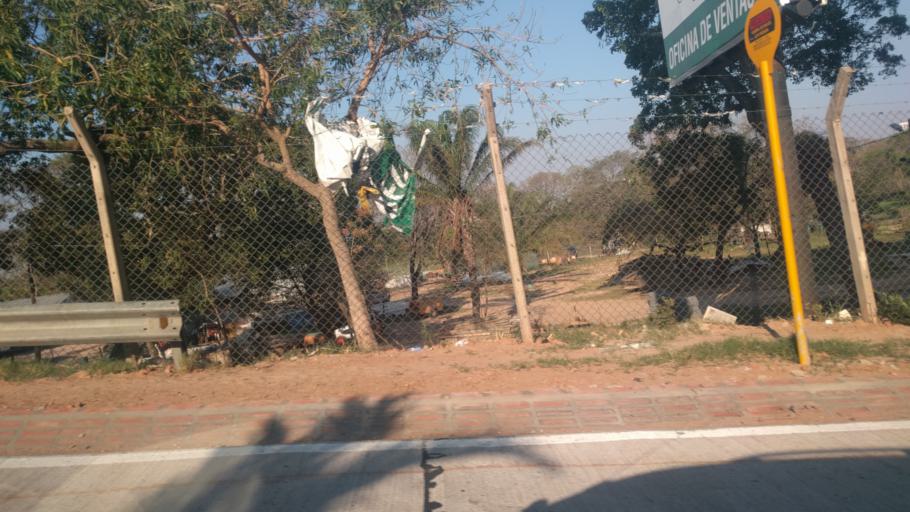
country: BO
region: Santa Cruz
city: Santa Cruz de la Sierra
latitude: -17.7509
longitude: -63.2162
